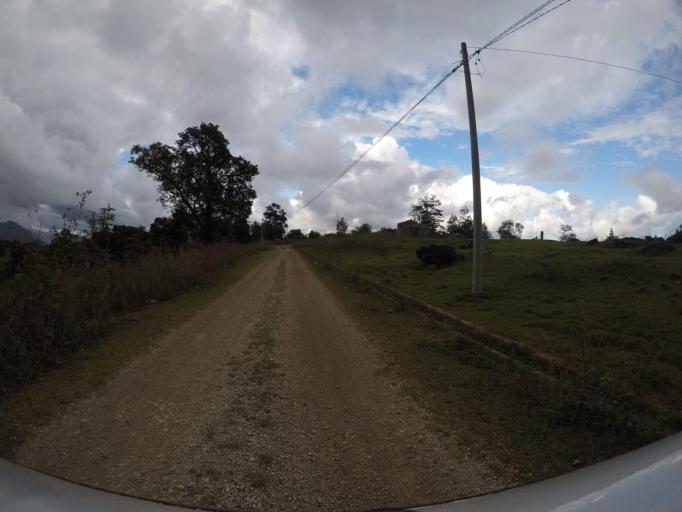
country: TL
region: Baucau
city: Venilale
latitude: -8.6712
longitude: 126.6326
